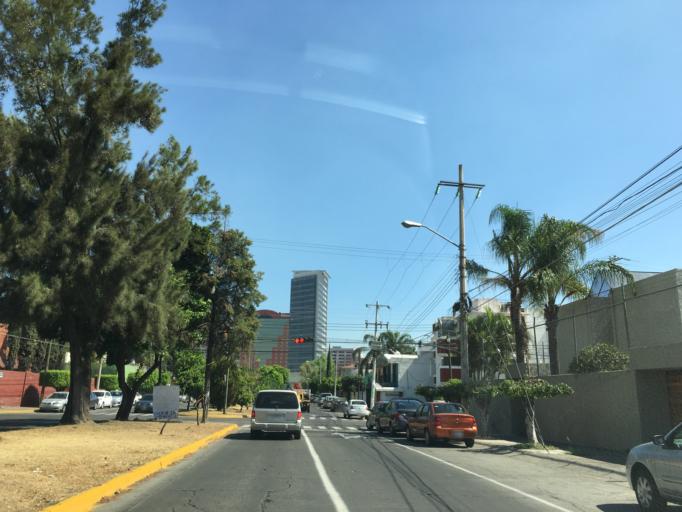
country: MX
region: Jalisco
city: Guadalajara
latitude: 20.6494
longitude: -103.3895
